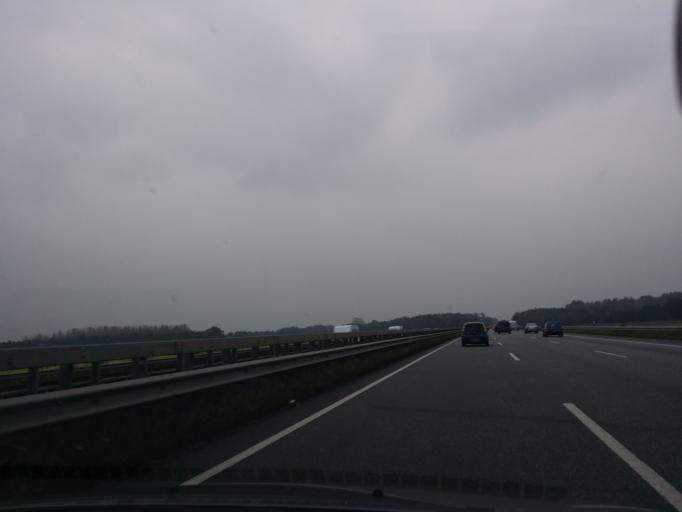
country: DE
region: Lower Saxony
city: Dinklage
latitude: 52.6838
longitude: 8.1722
